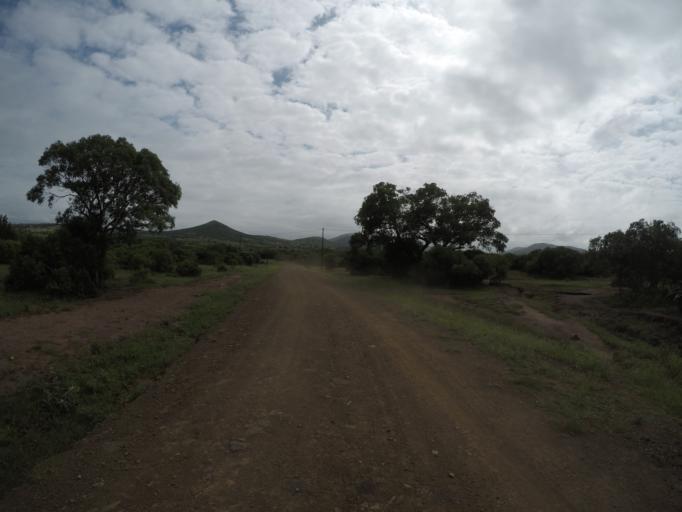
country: ZA
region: KwaZulu-Natal
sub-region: uThungulu District Municipality
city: Empangeni
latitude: -28.6227
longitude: 31.8557
